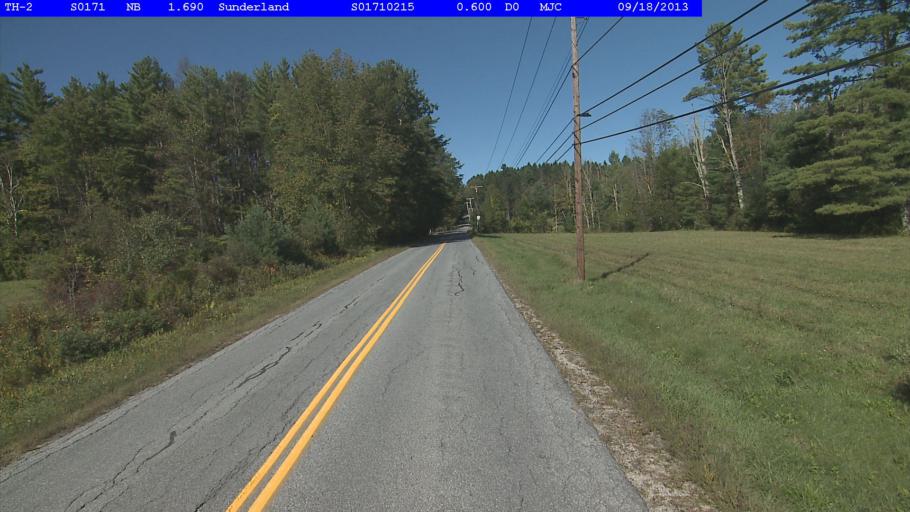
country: US
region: Vermont
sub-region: Bennington County
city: Arlington
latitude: 43.0744
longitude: -73.1309
